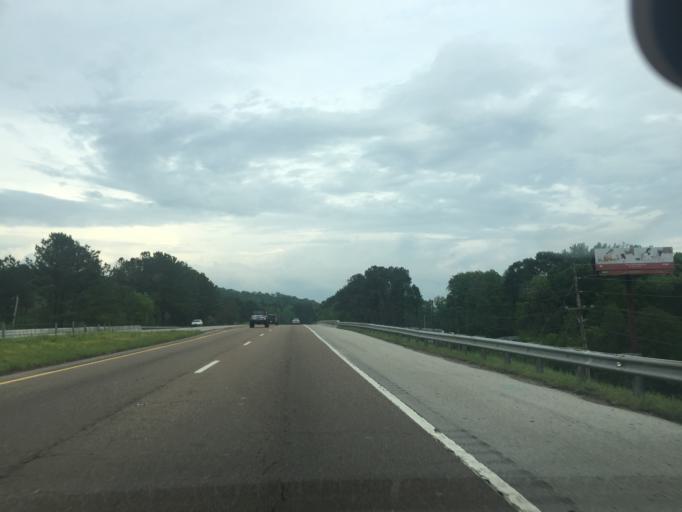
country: US
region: Tennessee
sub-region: Hamilton County
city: East Chattanooga
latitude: 35.1180
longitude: -85.2348
